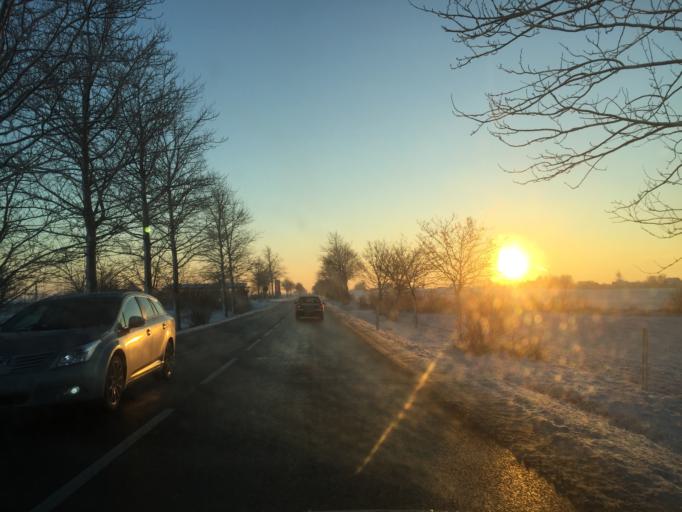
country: PL
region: Kujawsko-Pomorskie
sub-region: Powiat torunski
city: Lubicz Gorny
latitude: 53.0937
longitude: 18.7770
